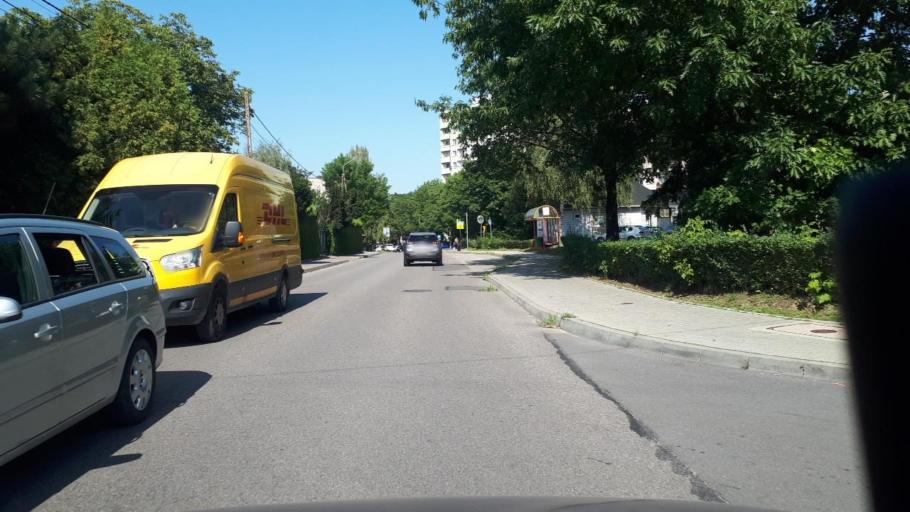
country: PL
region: Silesian Voivodeship
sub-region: Powiat bielski
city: Czechowice-Dziedzice
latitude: 49.9236
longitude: 19.0003
